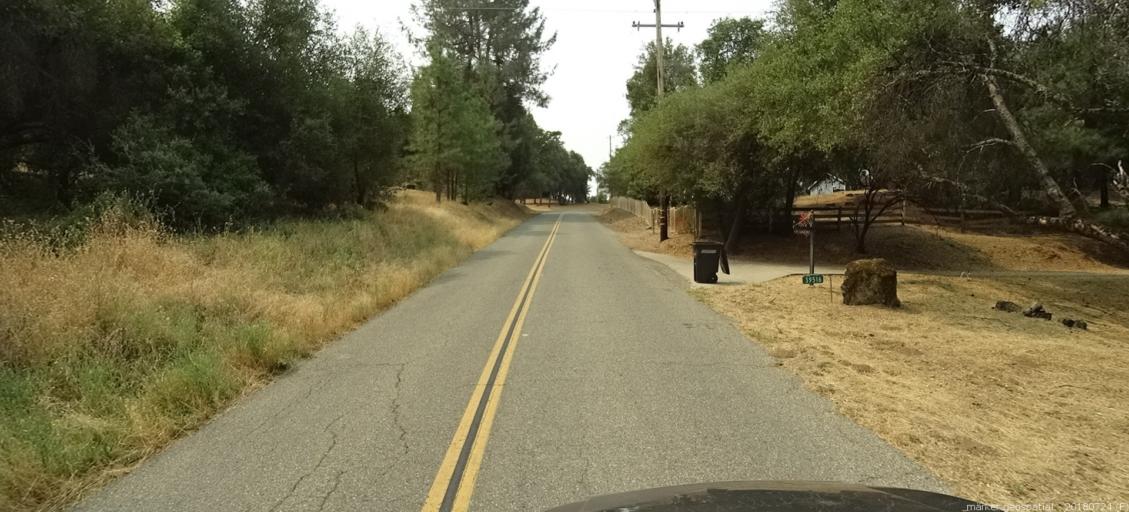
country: US
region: California
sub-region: Madera County
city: Oakhurst
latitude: 37.3228
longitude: -119.6172
